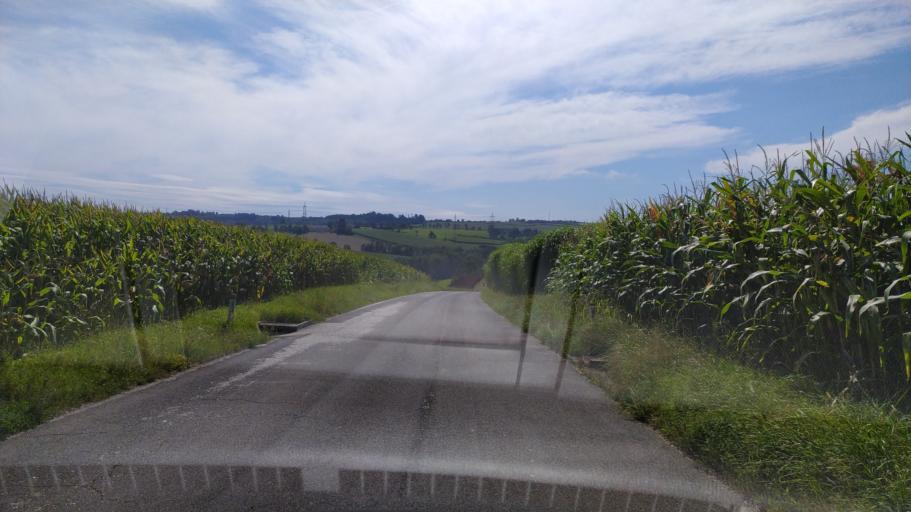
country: AT
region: Lower Austria
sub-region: Politischer Bezirk Amstetten
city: Strengberg
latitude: 48.1381
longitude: 14.6458
